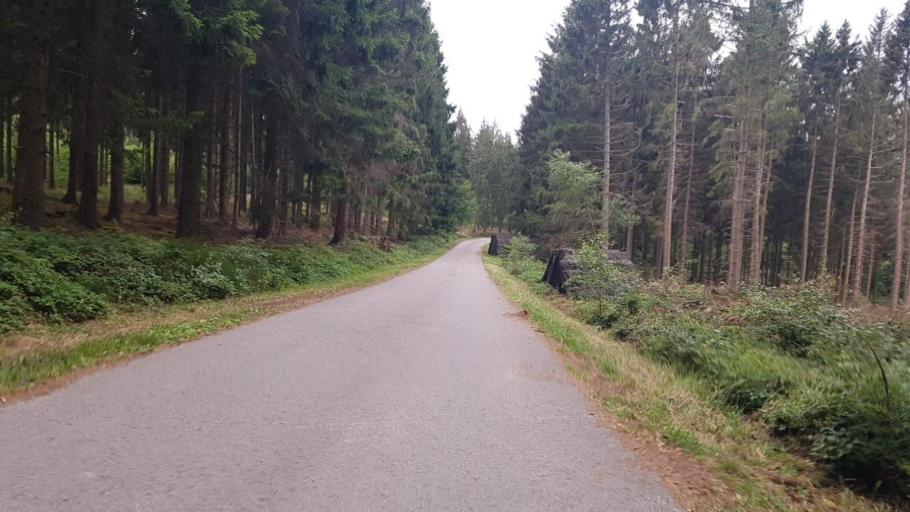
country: DE
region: North Rhine-Westphalia
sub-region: Regierungsbezirk Koln
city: Hurtgenwald
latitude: 50.7423
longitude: 6.3856
